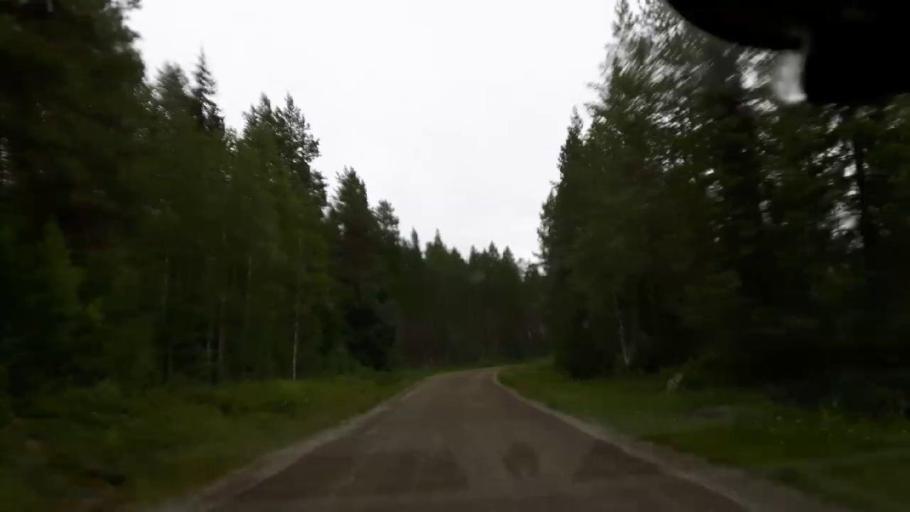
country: SE
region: Jaemtland
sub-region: Braecke Kommun
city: Braecke
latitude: 62.9469
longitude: 15.4452
